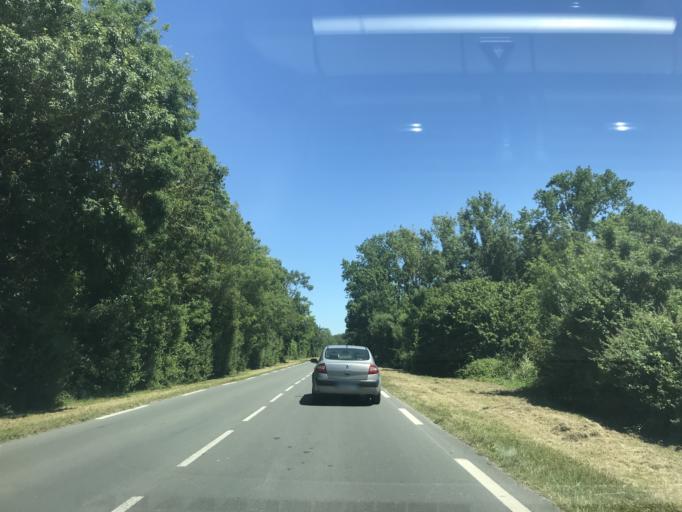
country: FR
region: Poitou-Charentes
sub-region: Departement de la Charente-Maritime
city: Meschers-sur-Gironde
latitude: 45.5644
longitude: -0.9520
